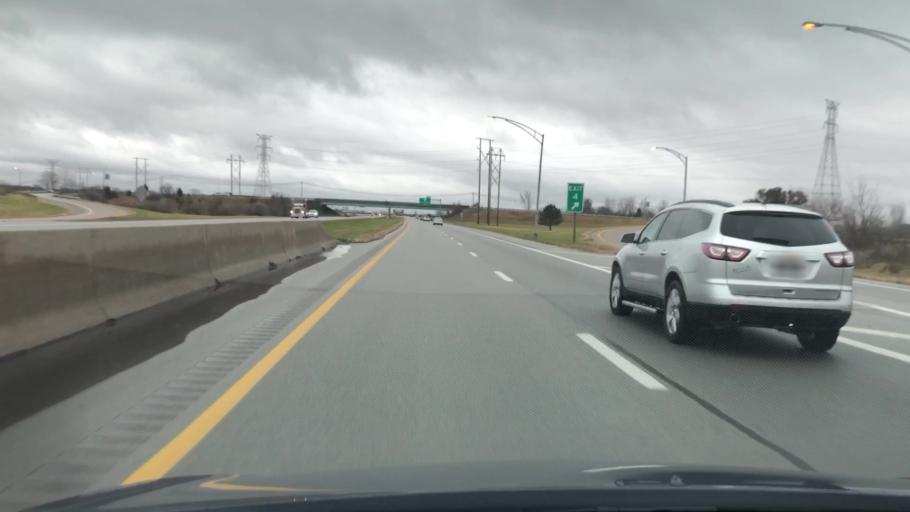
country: US
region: Ohio
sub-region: Wood County
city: Walbridge
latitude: 41.5910
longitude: -83.4770
